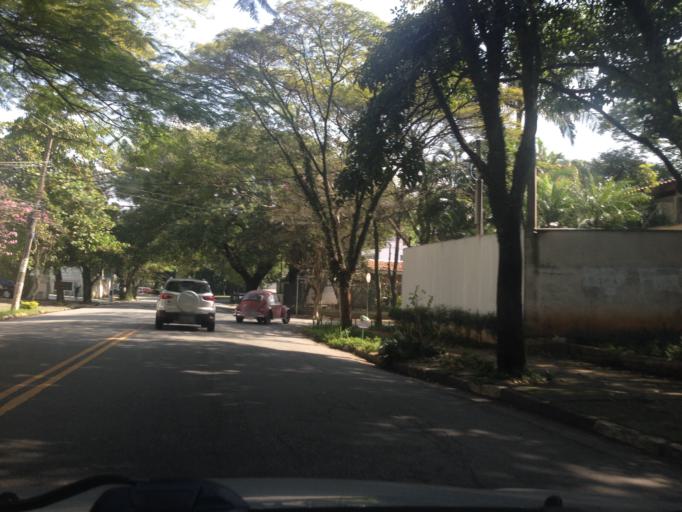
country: BR
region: Sao Paulo
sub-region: Sao Paulo
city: Sao Paulo
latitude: -23.5459
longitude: -46.7091
